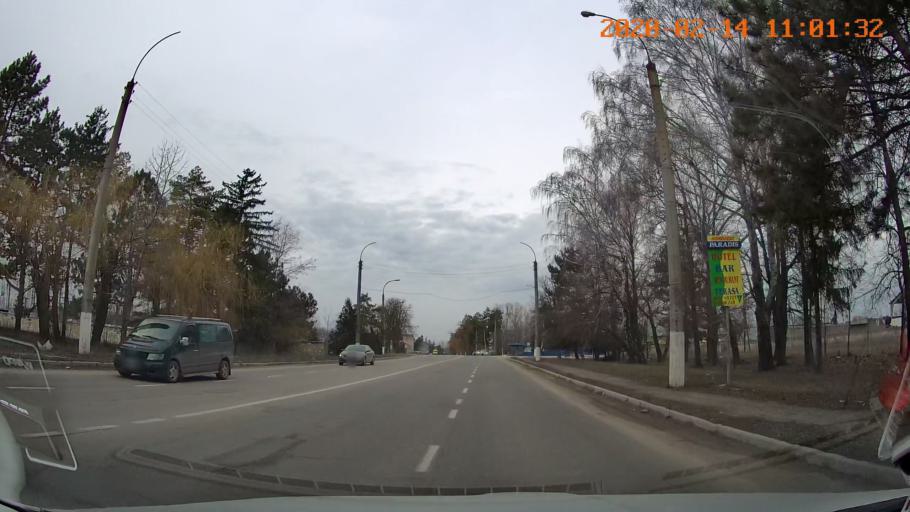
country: MD
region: Raionul Edinet
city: Edinet
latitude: 48.1604
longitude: 27.3283
